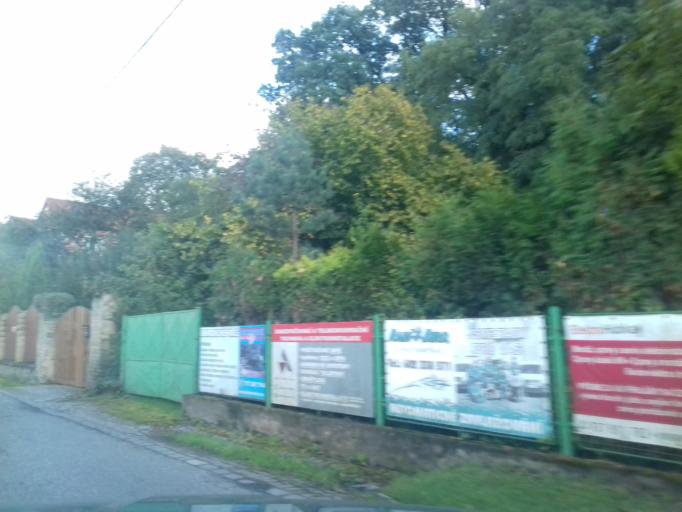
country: CZ
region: Central Bohemia
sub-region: Okres Praha-Zapad
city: Dobrichovice
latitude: 49.9249
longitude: 14.2771
